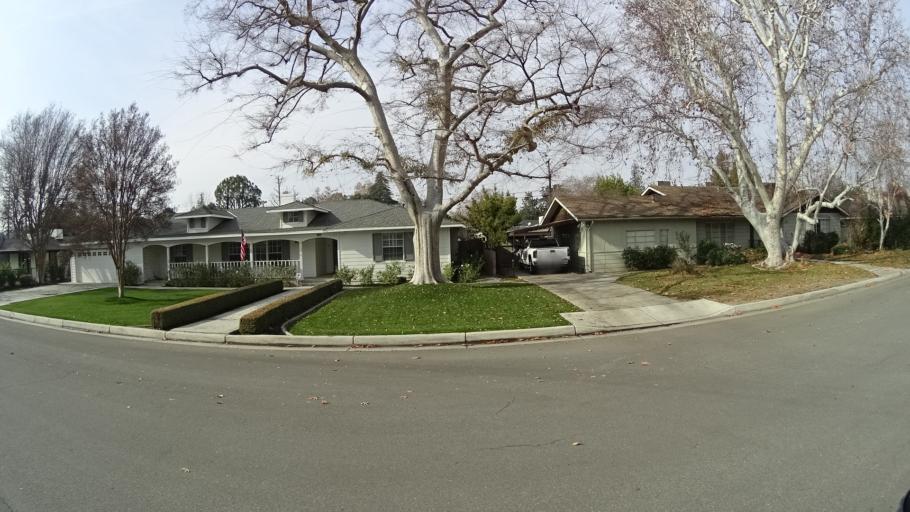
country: US
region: California
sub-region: Kern County
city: Bakersfield
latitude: 35.3801
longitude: -119.0340
